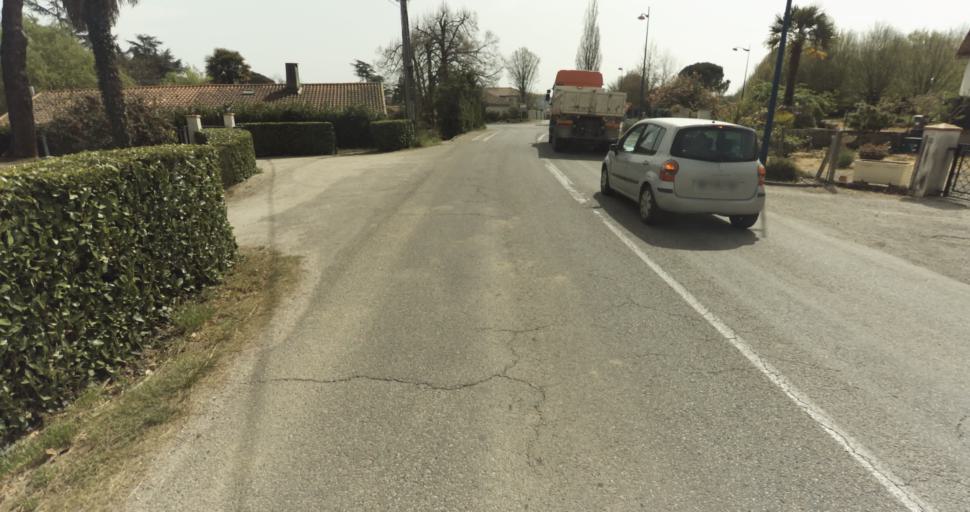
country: FR
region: Midi-Pyrenees
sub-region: Departement du Tarn-et-Garonne
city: Moissac
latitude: 44.1169
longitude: 1.1057
